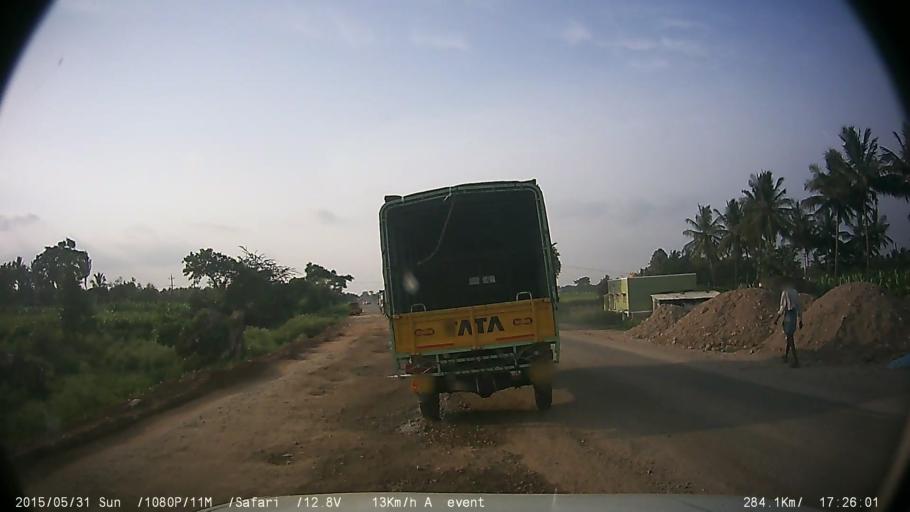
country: IN
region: Karnataka
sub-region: Chamrajnagar
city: Gundlupet
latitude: 11.8531
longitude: 76.6711
